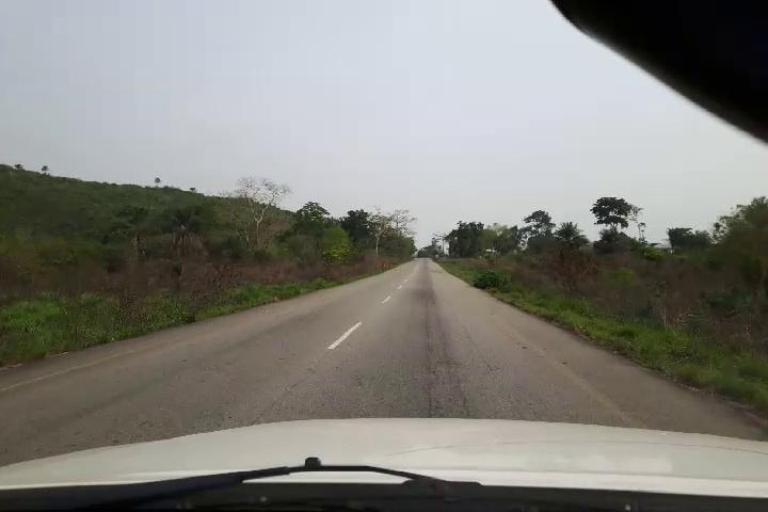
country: SL
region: Southern Province
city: Bo
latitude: 8.0087
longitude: -11.7773
